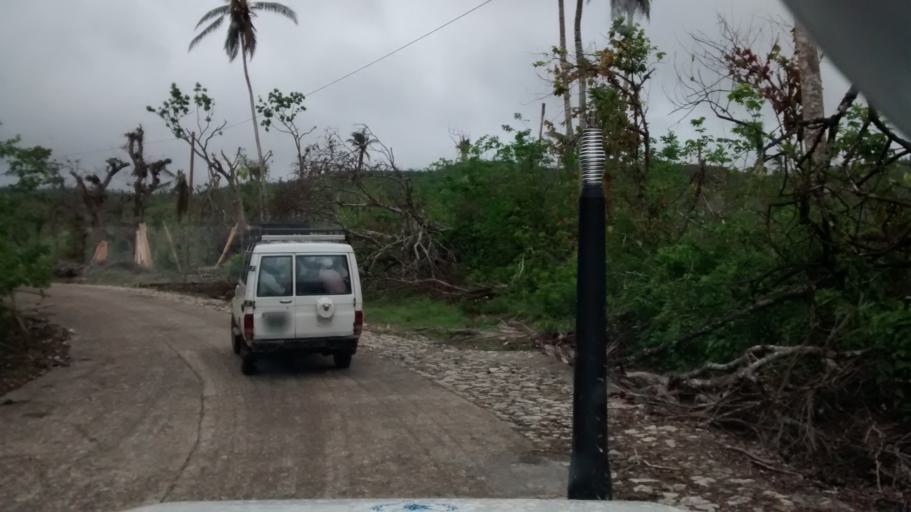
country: HT
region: Grandans
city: Moron
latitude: 18.5987
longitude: -74.1896
